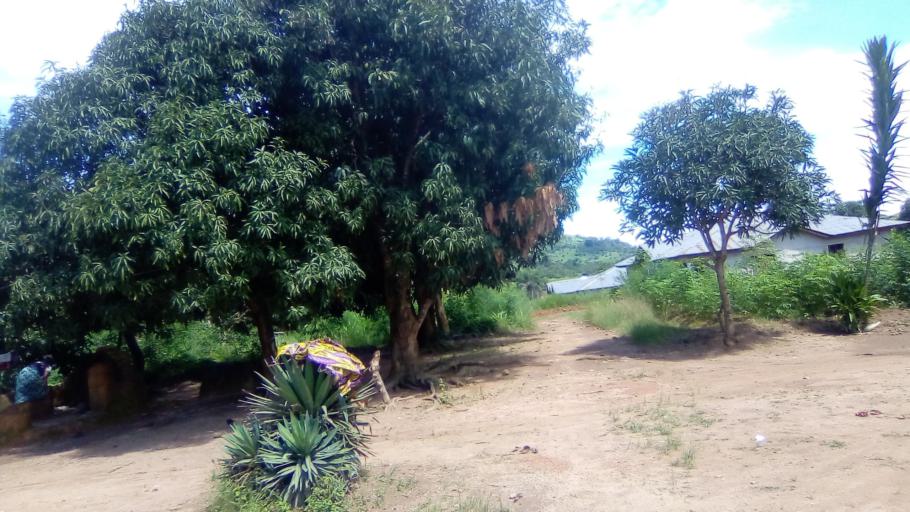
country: SL
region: Eastern Province
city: Simbakoro
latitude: 8.6369
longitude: -10.9979
